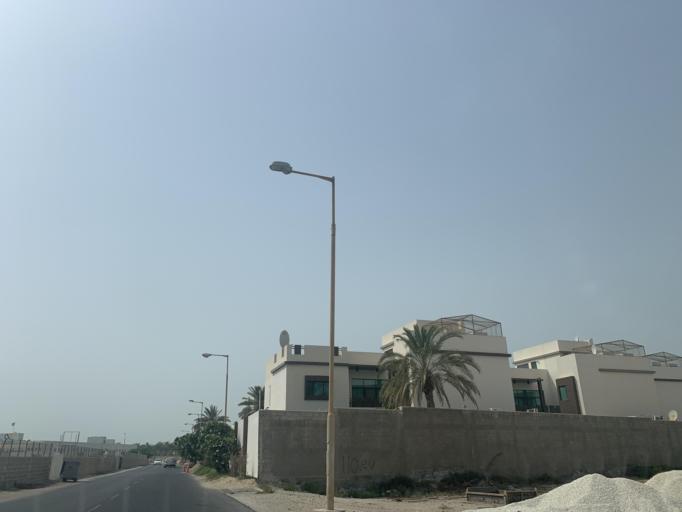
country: BH
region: Manama
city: Jidd Hafs
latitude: 26.1989
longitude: 50.4725
